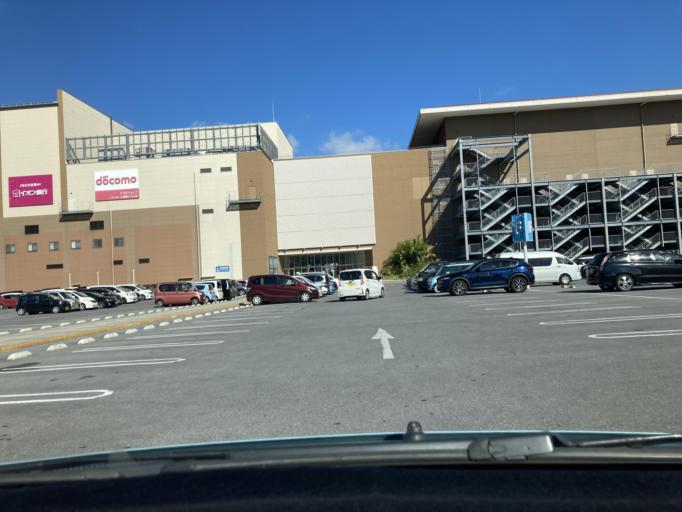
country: JP
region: Okinawa
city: Okinawa
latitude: 26.3131
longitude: 127.7967
